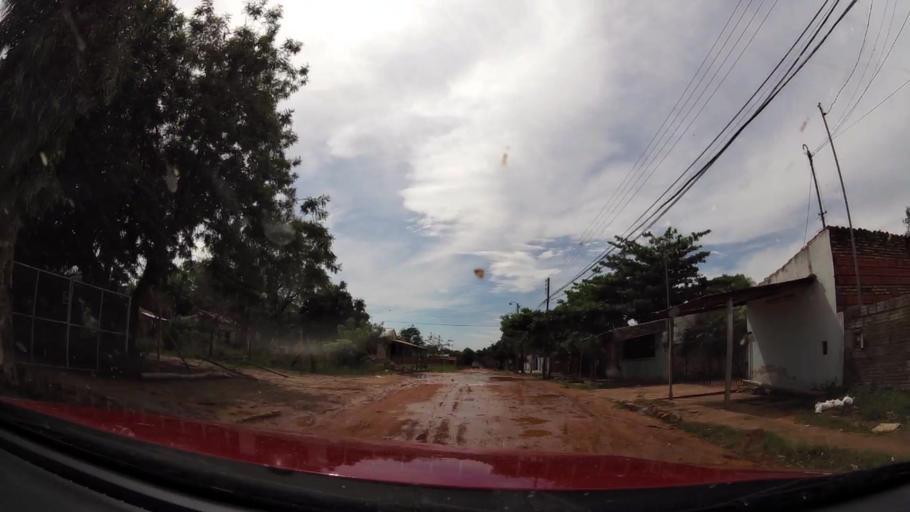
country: PY
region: Central
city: Limpio
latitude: -25.1887
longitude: -57.4773
